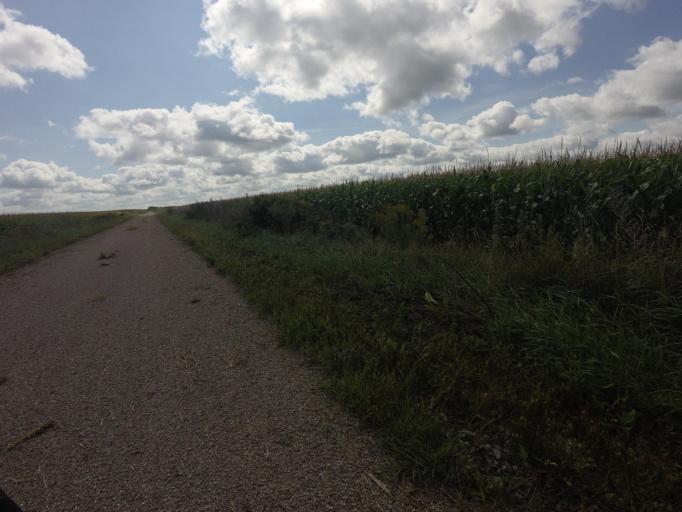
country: CA
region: Ontario
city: Huron East
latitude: 43.6455
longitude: -81.2155
